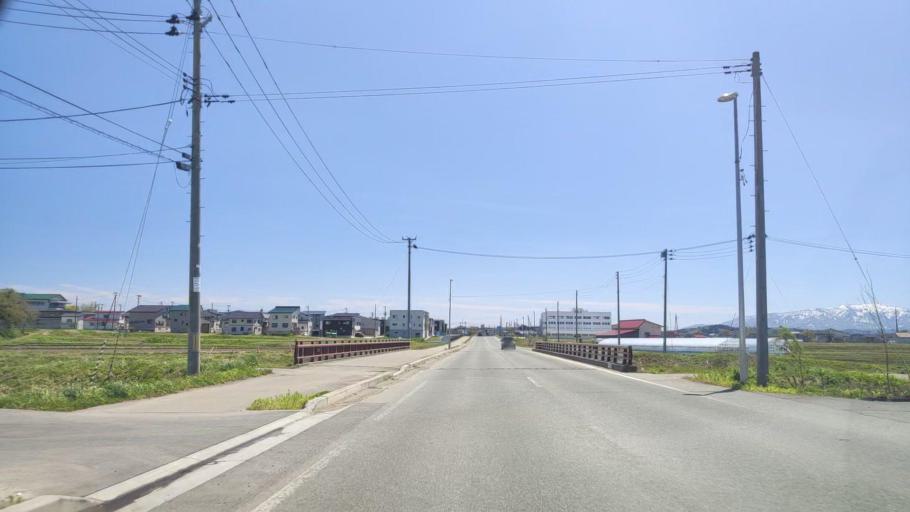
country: JP
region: Yamagata
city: Shinjo
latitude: 38.7559
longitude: 140.2939
